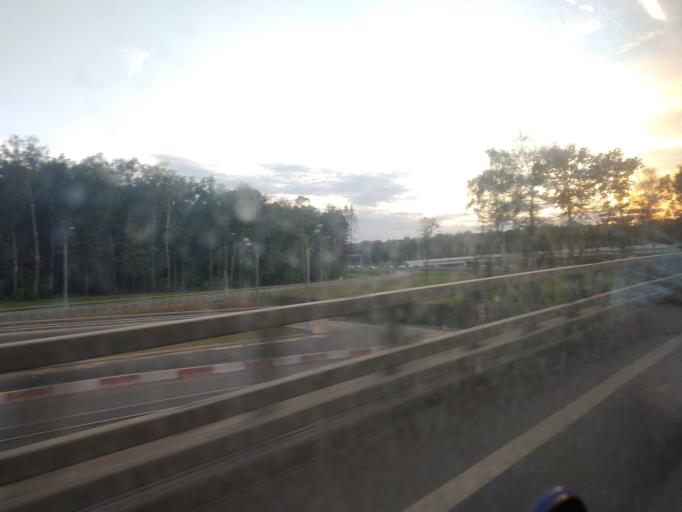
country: RU
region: Moscow
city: Solntsevo
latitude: 55.6136
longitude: 37.3786
